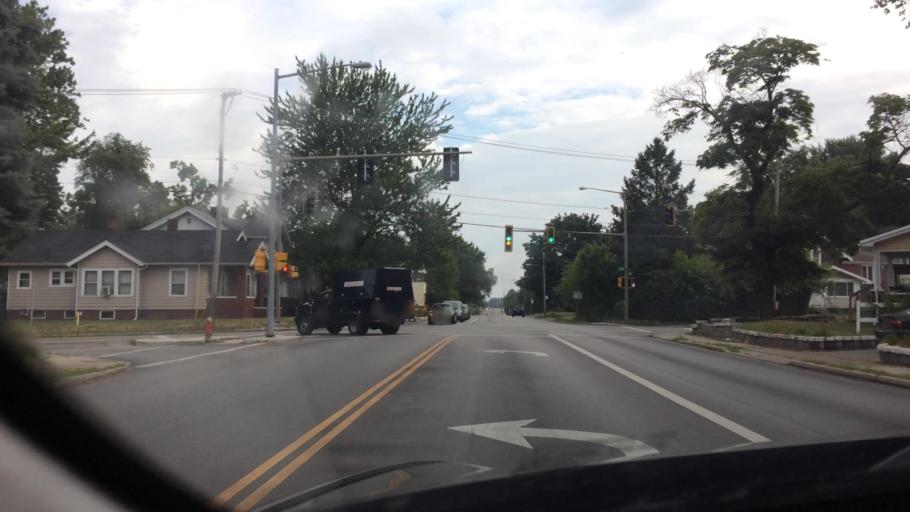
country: US
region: Ohio
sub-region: Wood County
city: Rossford
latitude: 41.6311
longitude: -83.5918
